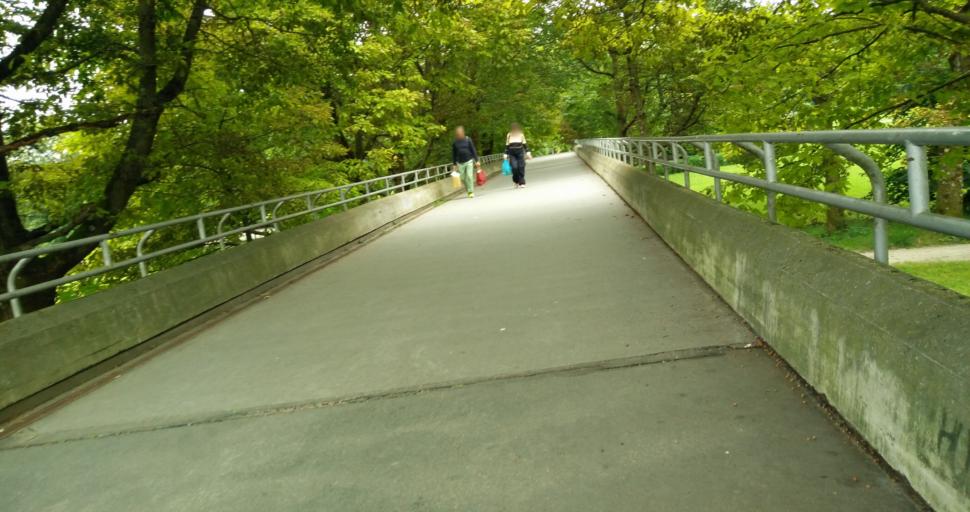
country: SI
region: Ljubljana
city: Ljubljana
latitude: 46.0572
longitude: 14.4973
